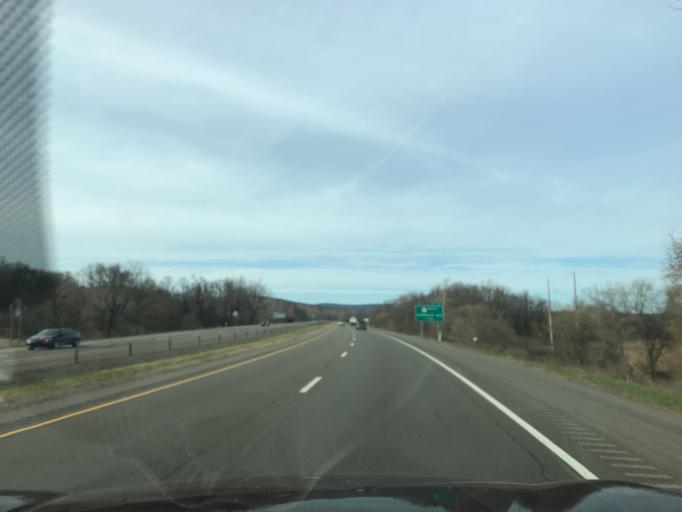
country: US
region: Pennsylvania
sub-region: Lycoming County
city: Montoursville
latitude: 41.2541
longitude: -76.9312
